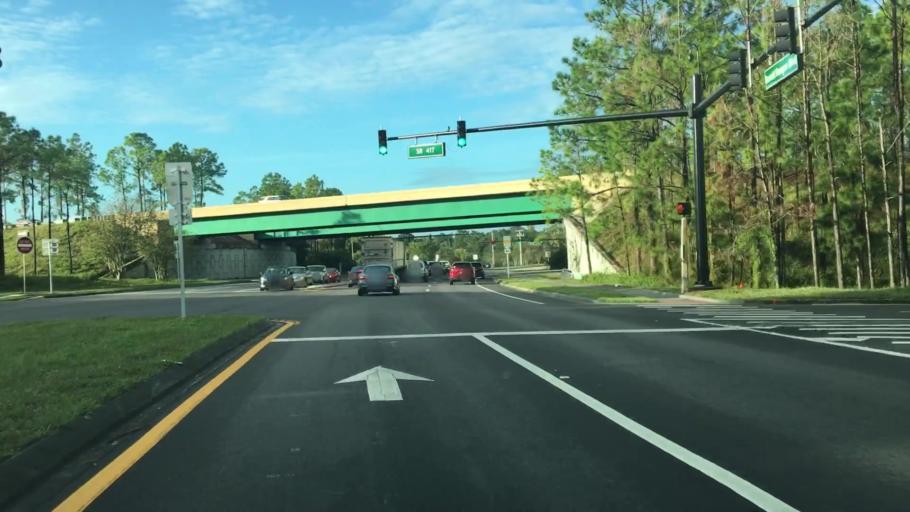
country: US
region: Florida
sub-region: Seminole County
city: Sanford
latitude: 28.7578
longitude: -81.2680
